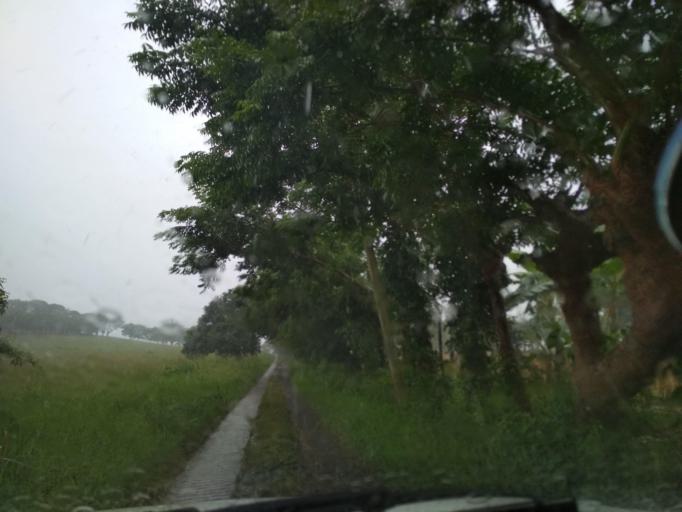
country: MX
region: Veracruz
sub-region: San Andres Tuxtla
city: Soyata
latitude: 18.4129
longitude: -95.2993
